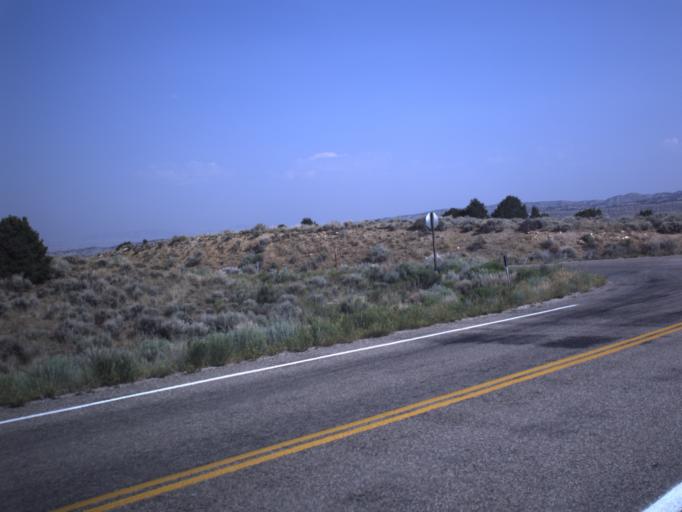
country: US
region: Utah
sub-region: Daggett County
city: Manila
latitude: 40.9617
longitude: -109.4695
